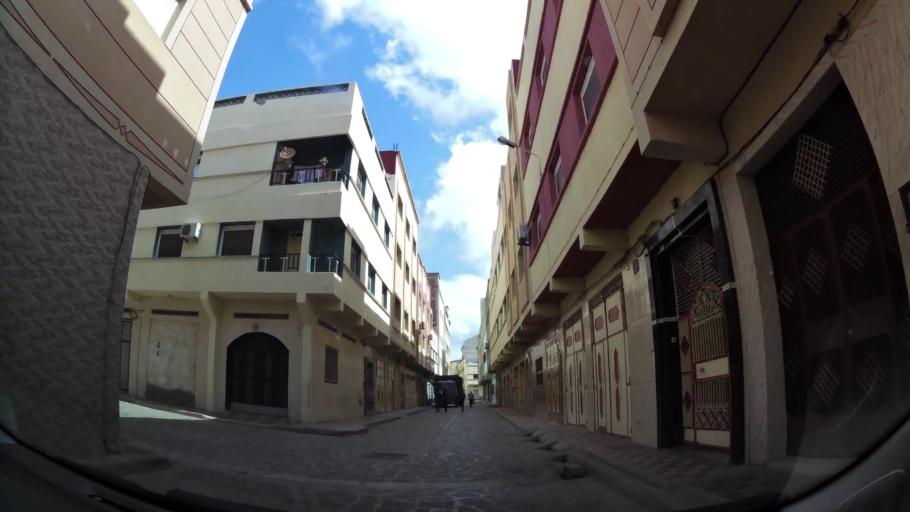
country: MA
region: Oriental
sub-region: Nador
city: Nador
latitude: 35.1622
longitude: -2.9298
